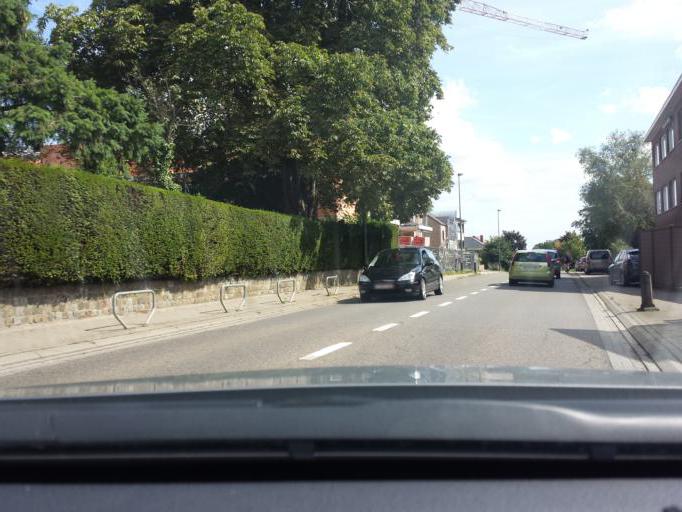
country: BE
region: Flanders
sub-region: Provincie Limburg
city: Beringen
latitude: 51.0475
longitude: 5.2239
